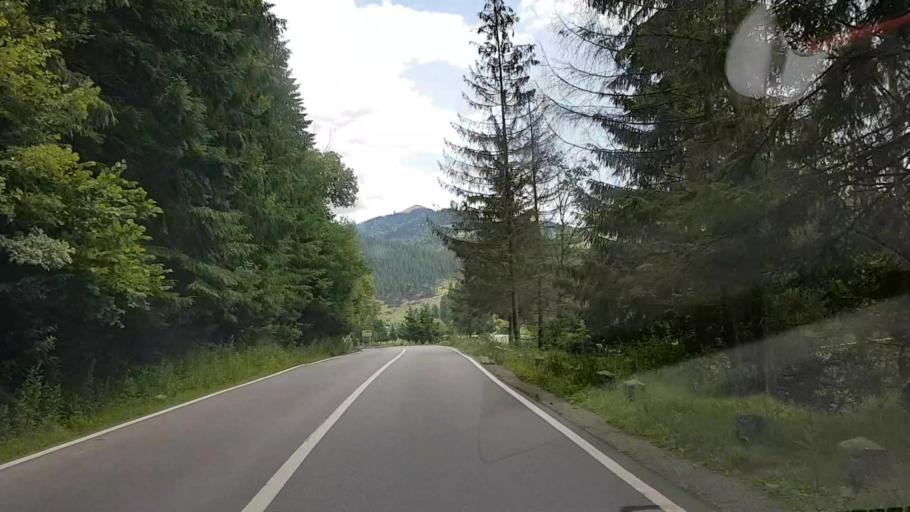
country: RO
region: Suceava
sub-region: Comuna Crucea
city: Crucea
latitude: 47.3618
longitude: 25.6043
